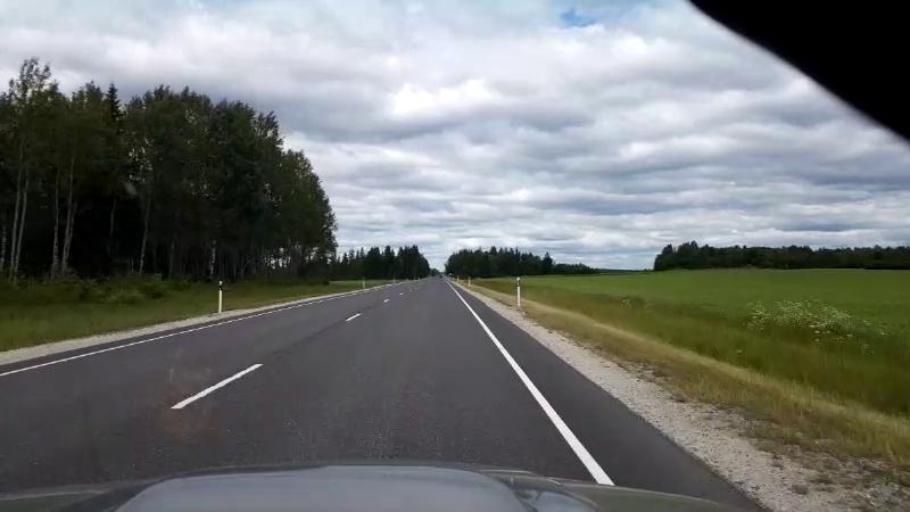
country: EE
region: Raplamaa
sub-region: Maerjamaa vald
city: Marjamaa
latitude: 58.8526
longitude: 24.4315
